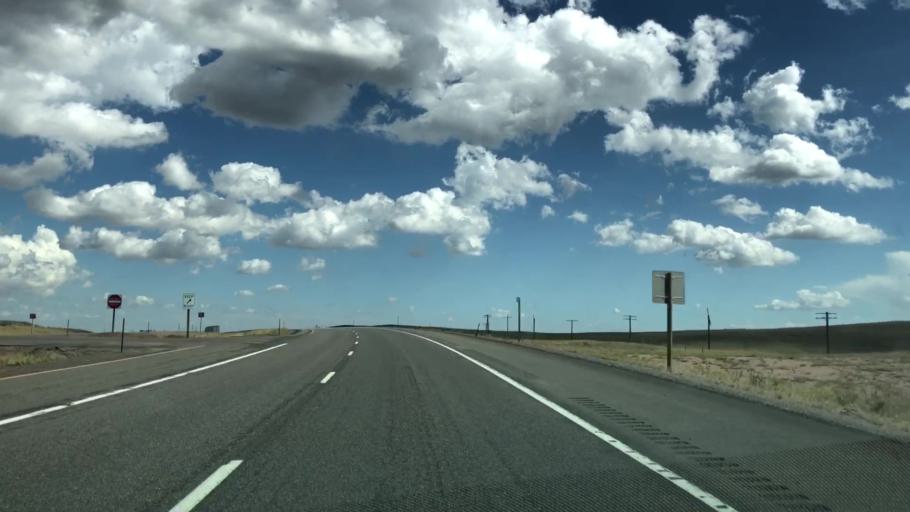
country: US
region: Wyoming
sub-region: Albany County
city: Laramie
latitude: 41.0310
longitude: -105.4378
